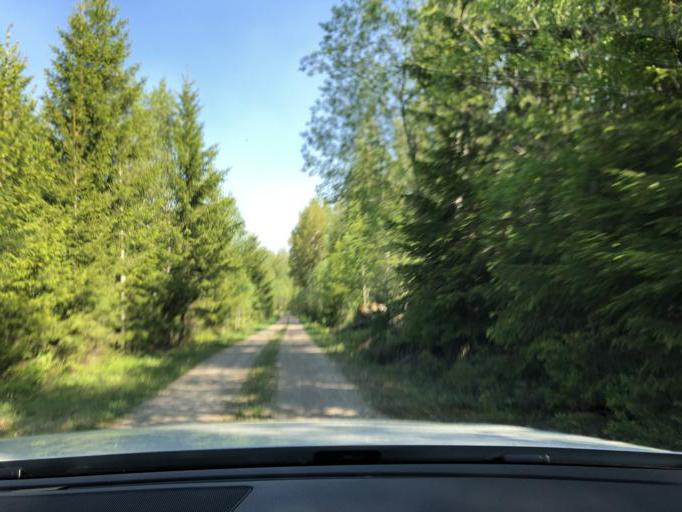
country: SE
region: Dalarna
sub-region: Avesta Kommun
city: Horndal
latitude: 60.2082
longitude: 16.4922
